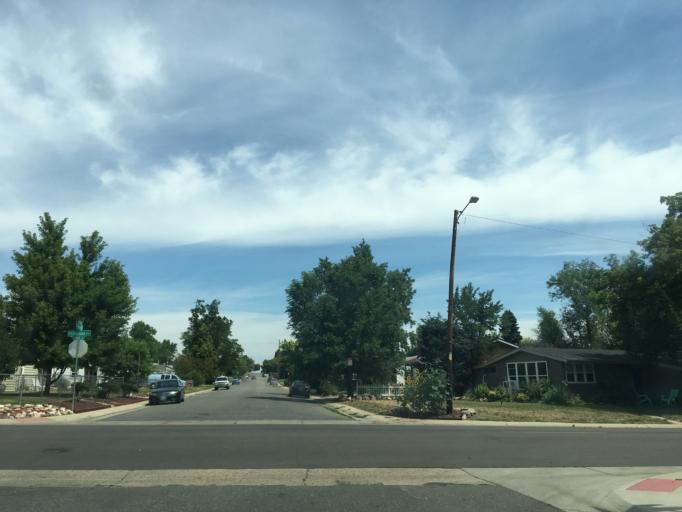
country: US
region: Colorado
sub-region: Jefferson County
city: Lakewood
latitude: 39.6929
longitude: -105.0425
